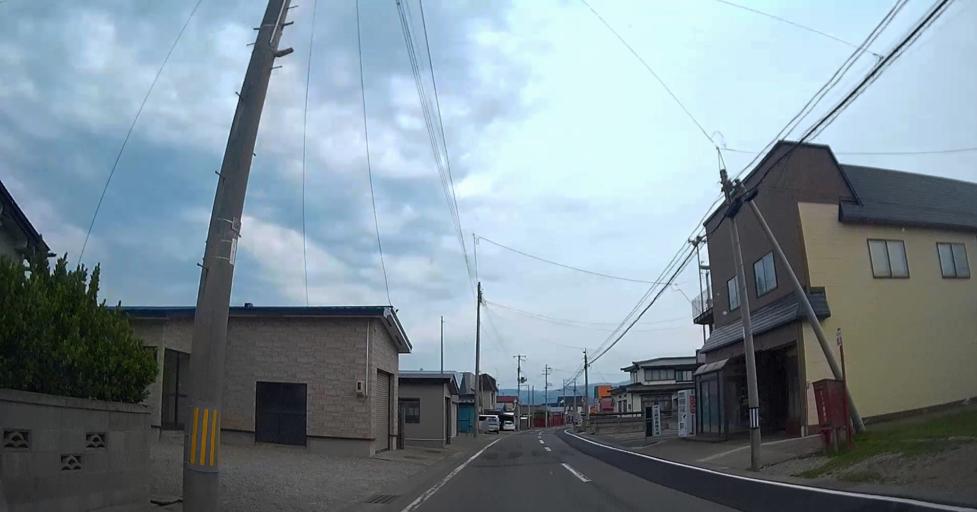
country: JP
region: Aomori
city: Shimokizukuri
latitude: 41.0301
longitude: 140.3263
